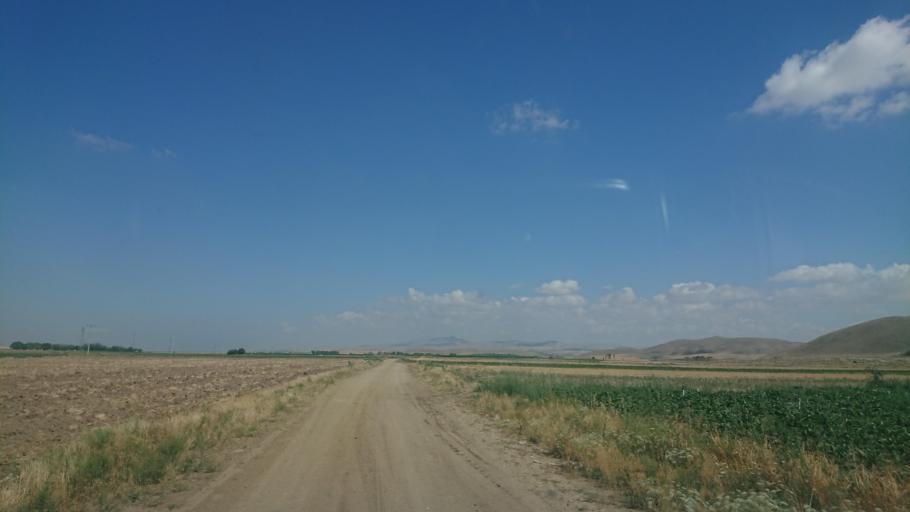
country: TR
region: Aksaray
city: Sariyahsi
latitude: 38.9786
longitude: 33.9108
